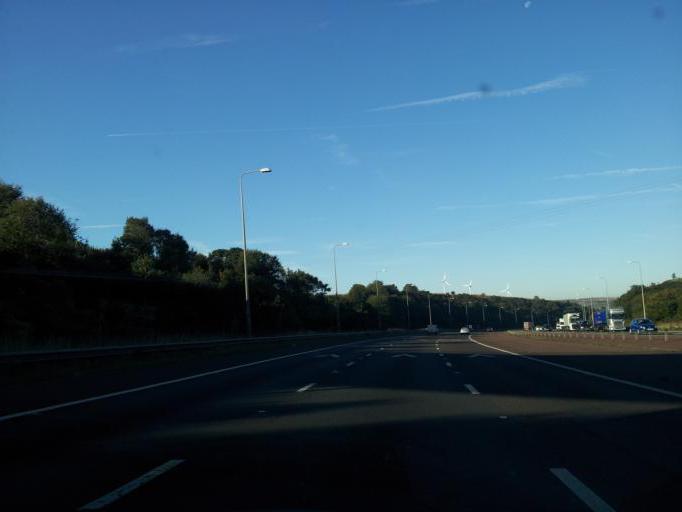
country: GB
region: England
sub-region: Kirklees
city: Linthwaite
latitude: 53.6446
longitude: -1.8950
